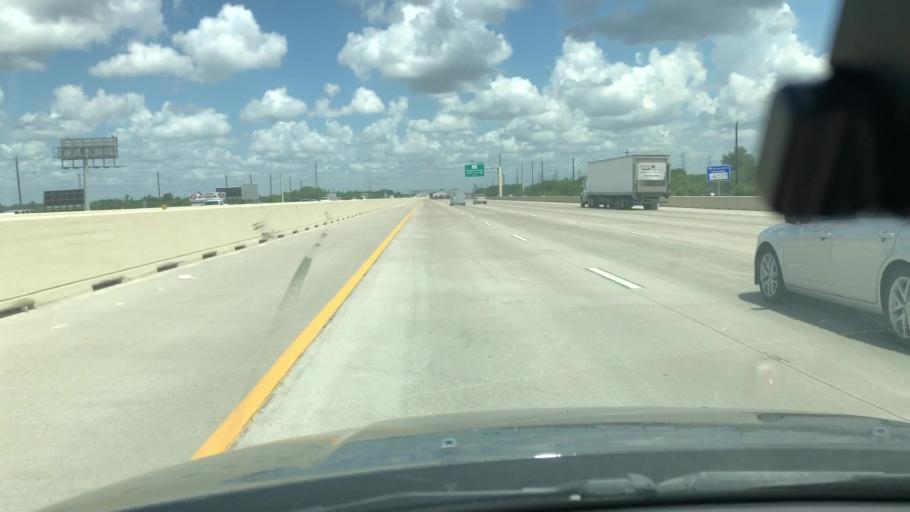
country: US
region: Texas
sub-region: Harris County
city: Webster
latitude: 29.5587
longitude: -95.1588
